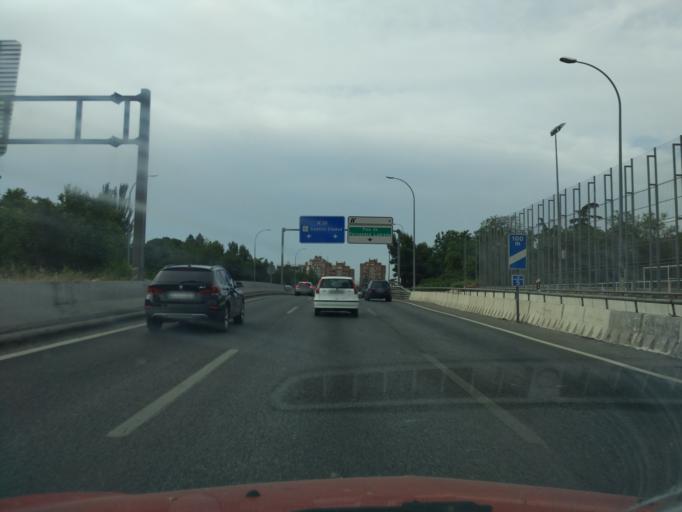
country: ES
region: Madrid
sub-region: Provincia de Madrid
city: Carabanchel
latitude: 40.3808
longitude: -3.7187
